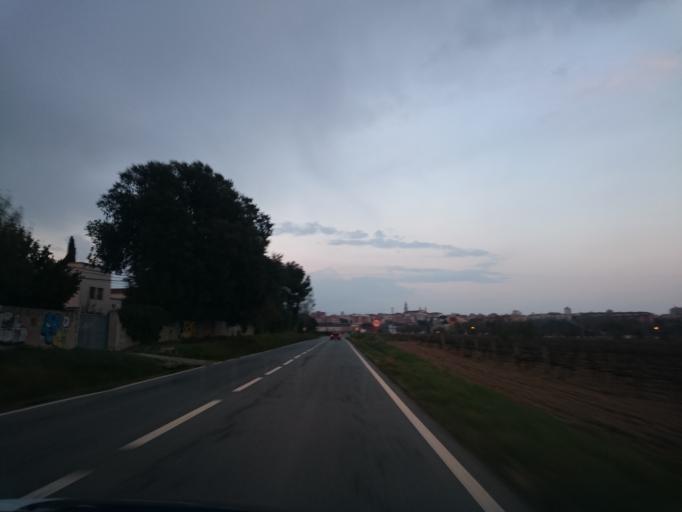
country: ES
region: Catalonia
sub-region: Provincia de Barcelona
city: Vilafranca del Penedes
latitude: 41.3513
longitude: 1.6838
